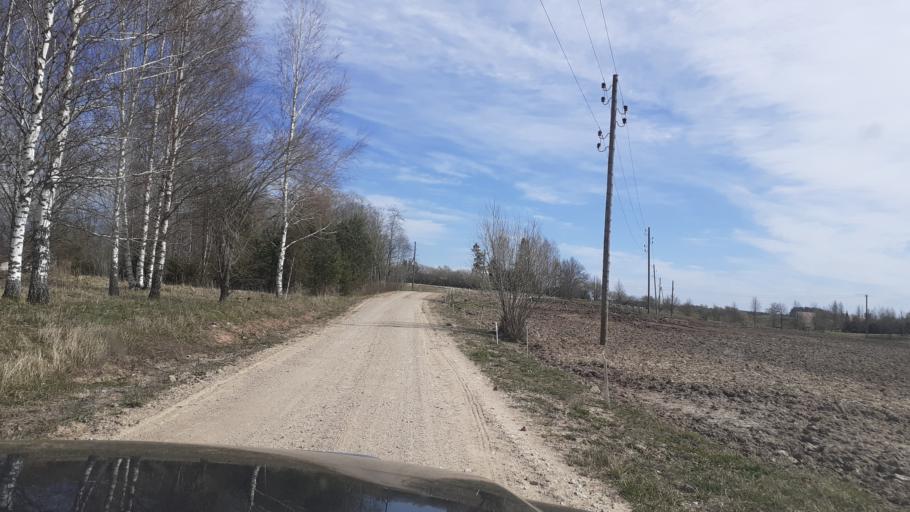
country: LV
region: Kuldigas Rajons
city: Kuldiga
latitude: 56.8375
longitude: 21.9958
